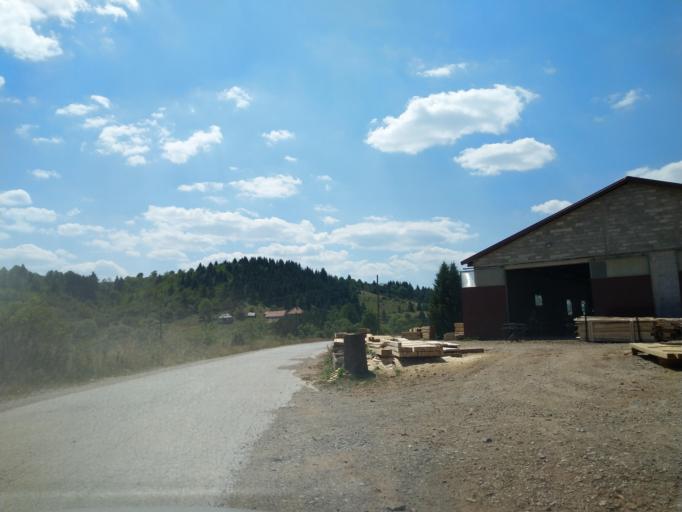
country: RS
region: Central Serbia
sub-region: Zlatiborski Okrug
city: Nova Varos
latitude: 43.4478
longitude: 19.9662
